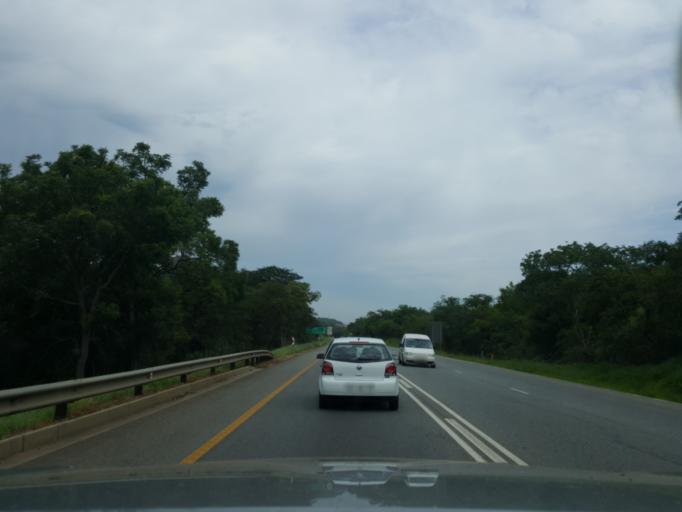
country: ZA
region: Mpumalanga
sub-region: Ehlanzeni District
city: Nelspruit
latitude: -25.5011
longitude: 31.1847
